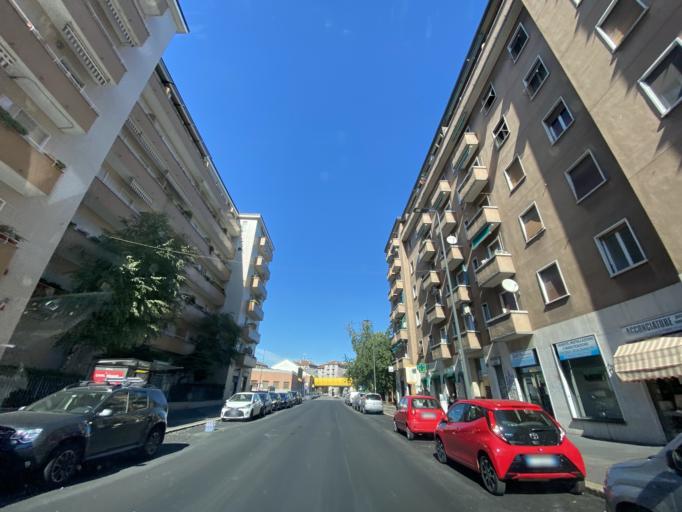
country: IT
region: Lombardy
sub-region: Citta metropolitana di Milano
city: Sesto San Giovanni
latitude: 45.4995
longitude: 9.2120
